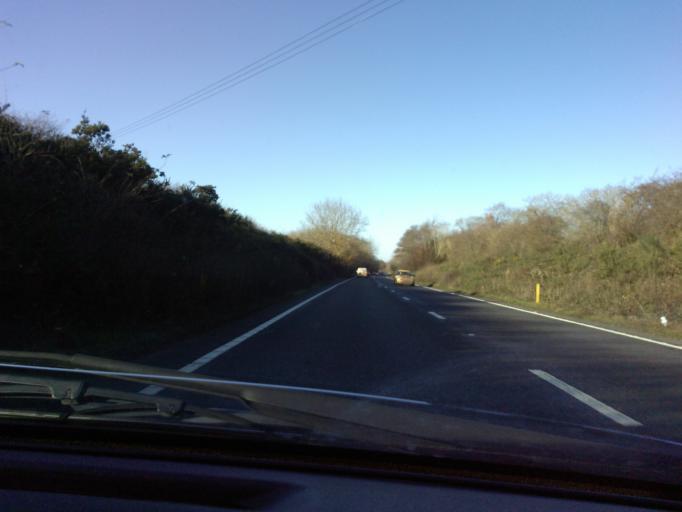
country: GB
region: England
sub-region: Dorset
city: Wimborne Minster
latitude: 50.7894
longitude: -1.9871
